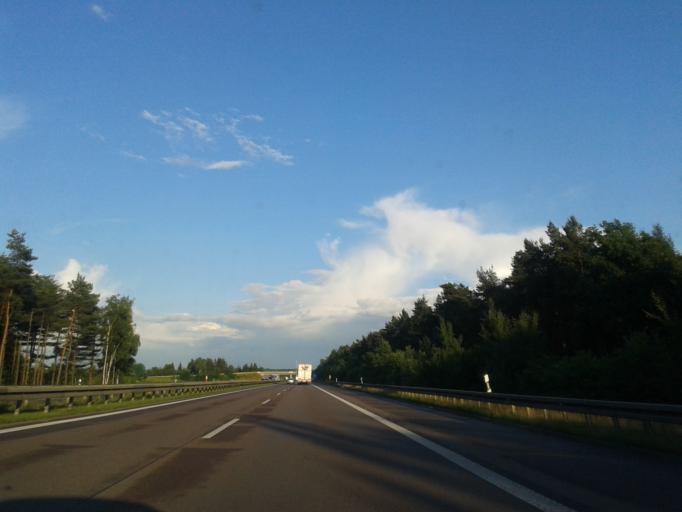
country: DE
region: Saxony
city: Naunhof
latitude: 51.2956
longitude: 12.6198
